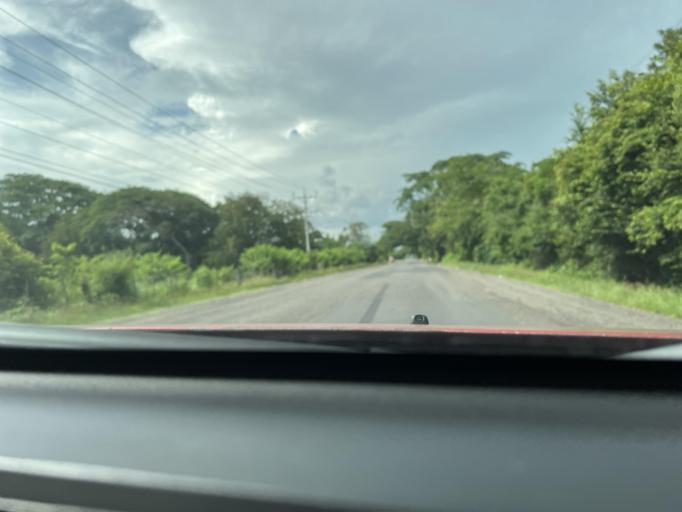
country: SV
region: La Union
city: San Alejo
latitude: 13.3826
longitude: -87.9060
